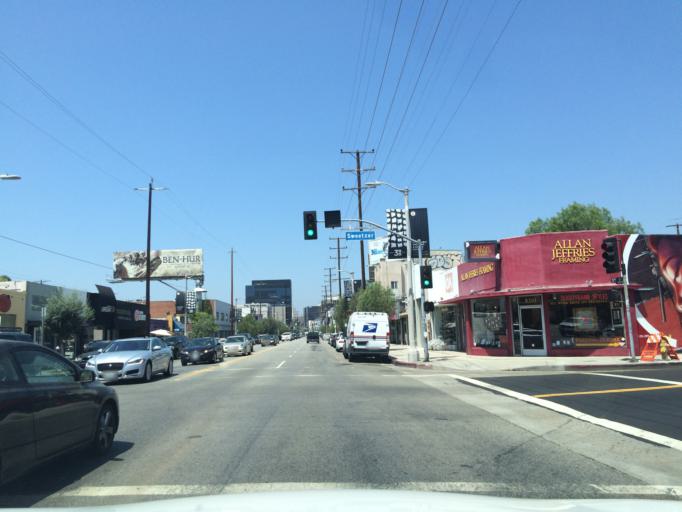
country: US
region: California
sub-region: Los Angeles County
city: West Hollywood
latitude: 34.0727
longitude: -118.3699
